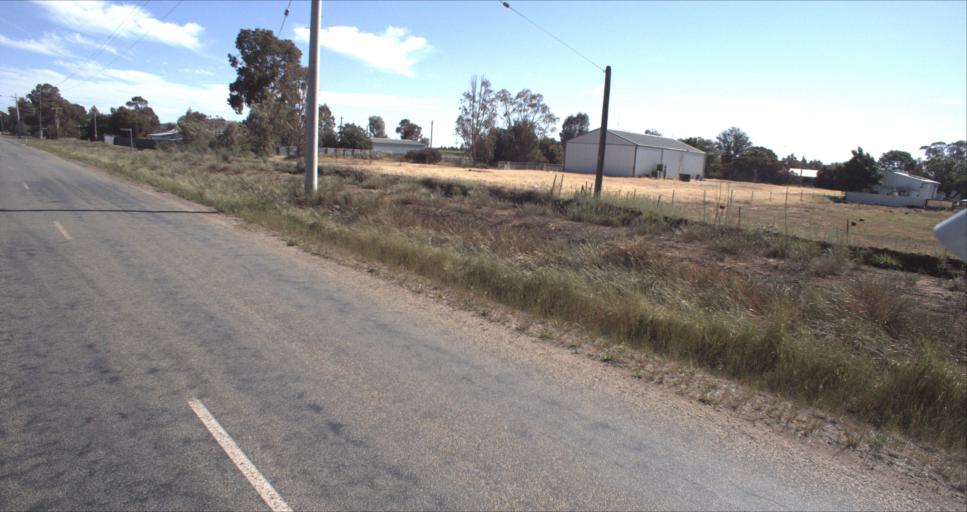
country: AU
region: New South Wales
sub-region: Leeton
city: Leeton
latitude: -34.5540
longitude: 146.3849
